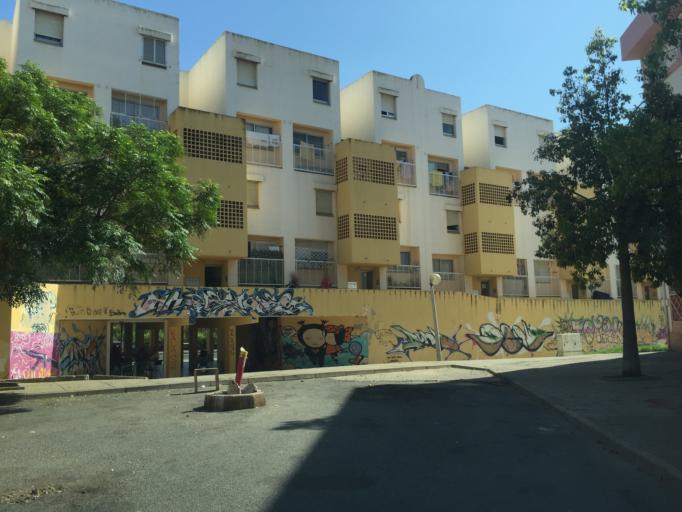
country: PT
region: Faro
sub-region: Olhao
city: Olhao
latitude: 37.0329
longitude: -7.8332
